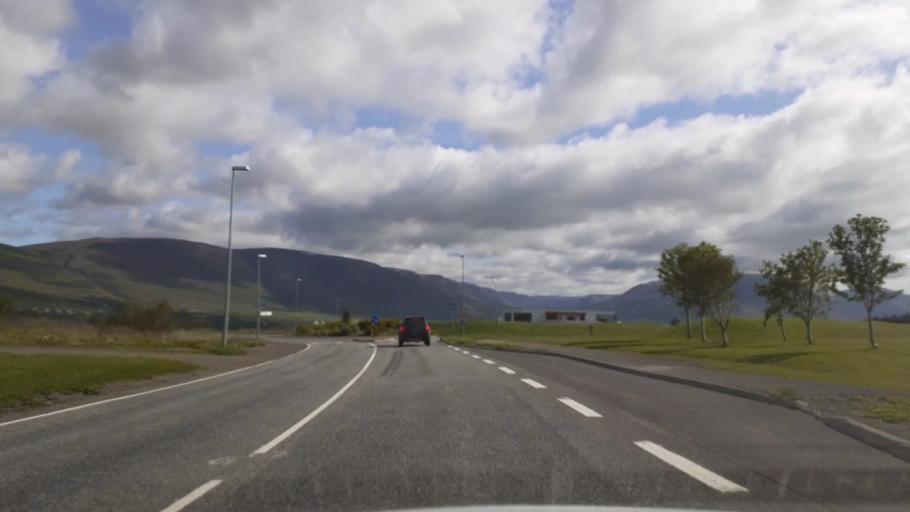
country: IS
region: Northeast
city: Akureyri
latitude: 65.6654
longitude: -18.0911
